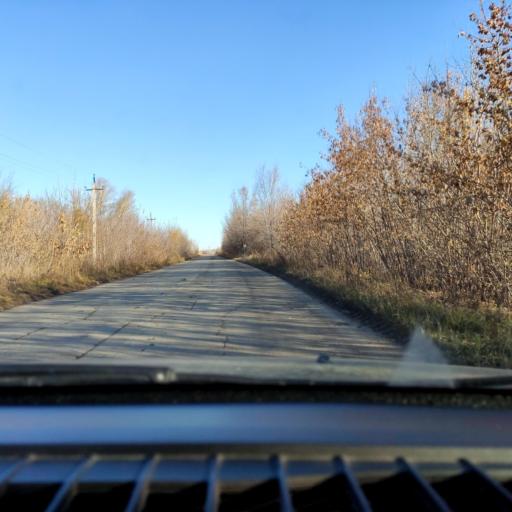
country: RU
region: Samara
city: Tol'yatti
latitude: 53.6401
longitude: 49.3142
